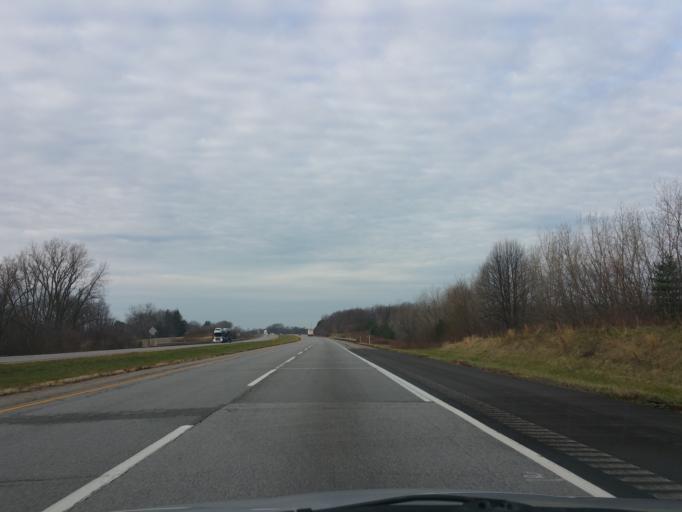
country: US
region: Indiana
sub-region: LaPorte County
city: LaPorte
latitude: 41.6745
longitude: -86.6886
